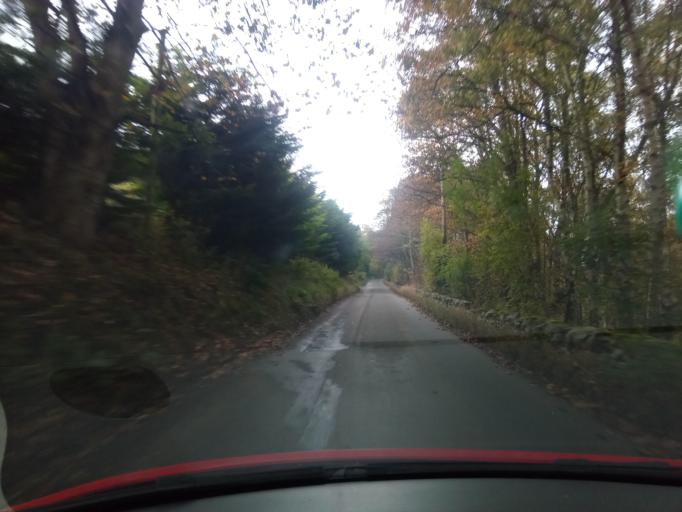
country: GB
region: Scotland
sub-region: The Scottish Borders
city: Peebles
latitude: 55.6335
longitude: -3.1284
